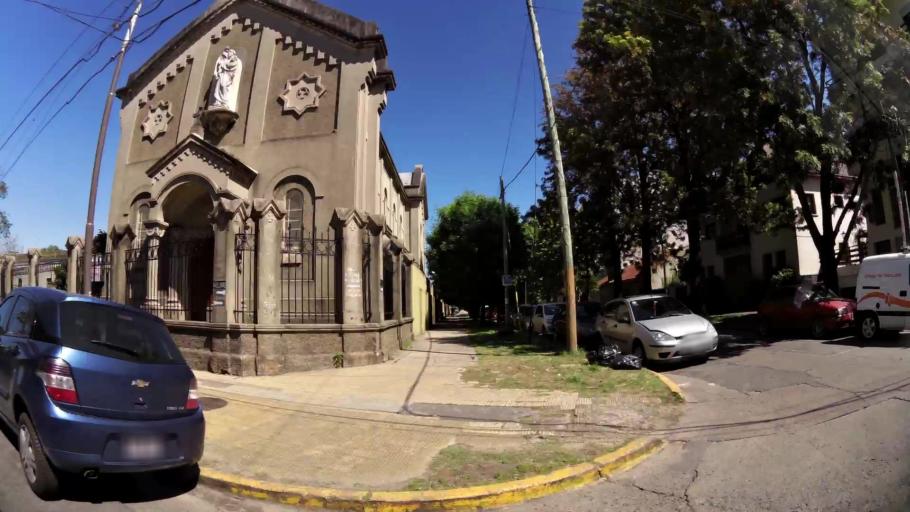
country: AR
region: Buenos Aires
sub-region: Partido de Quilmes
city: Quilmes
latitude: -34.7097
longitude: -58.2837
